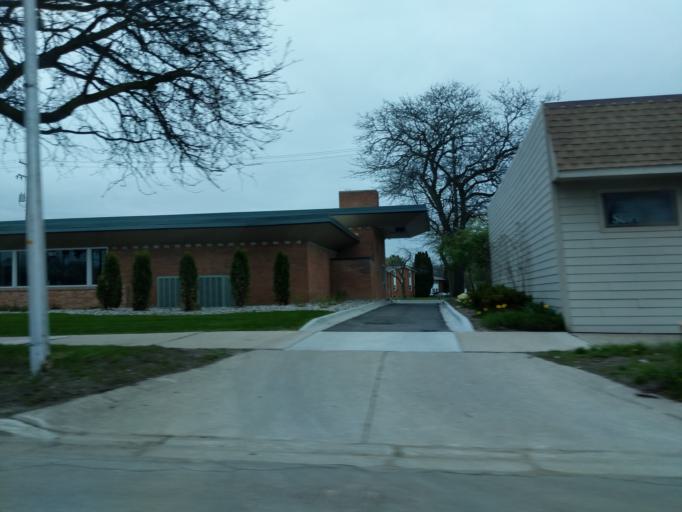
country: US
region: Michigan
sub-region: Midland County
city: Midland
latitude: 43.6238
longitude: -84.2241
